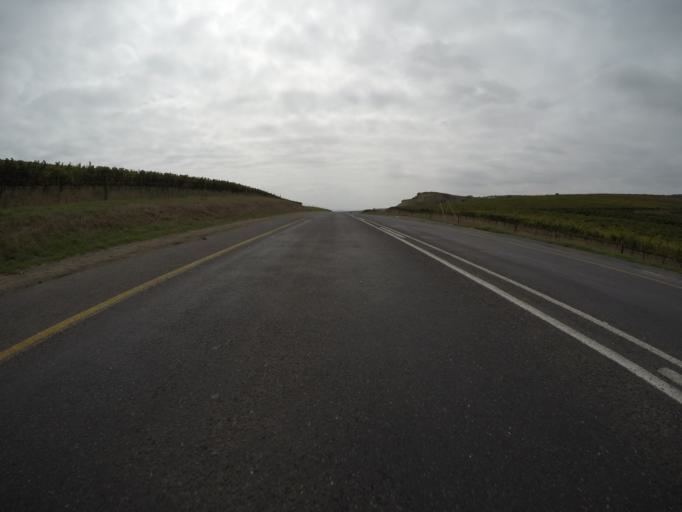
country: ZA
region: Western Cape
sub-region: City of Cape Town
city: Sunset Beach
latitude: -33.8342
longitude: 18.5906
